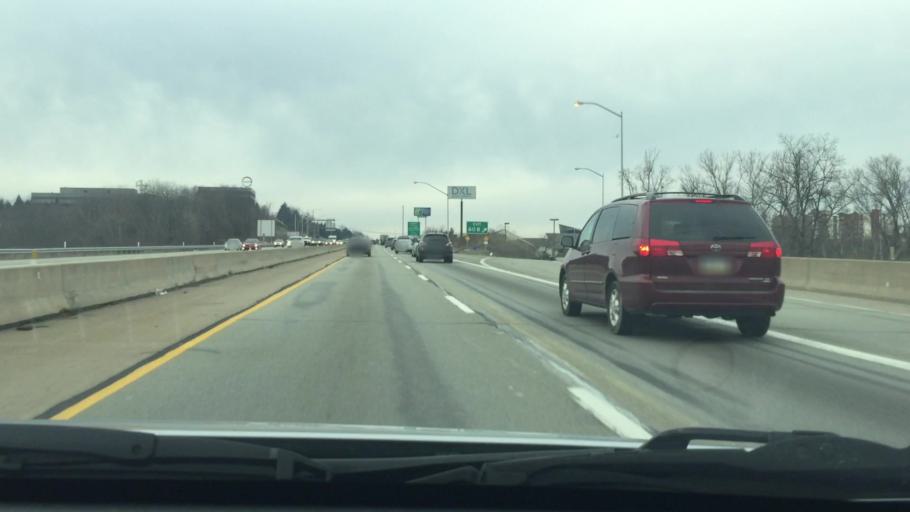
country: US
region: Pennsylvania
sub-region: Allegheny County
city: Rennerdale
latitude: 40.4414
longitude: -80.1576
